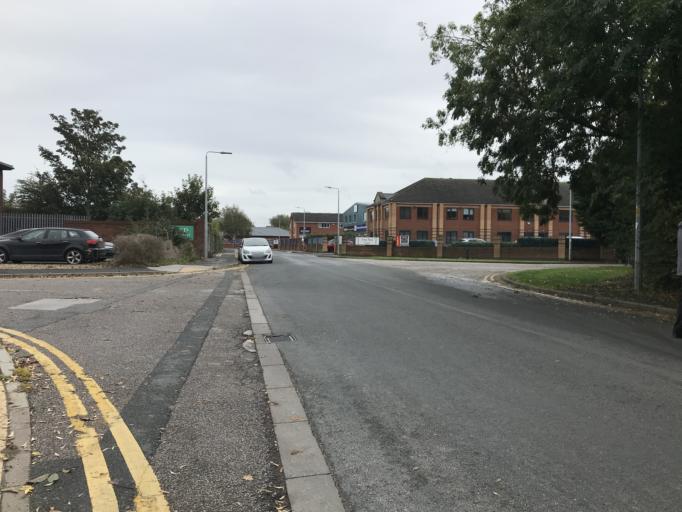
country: GB
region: England
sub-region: East Riding of Yorkshire
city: Beverley
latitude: 53.8403
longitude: -0.4018
